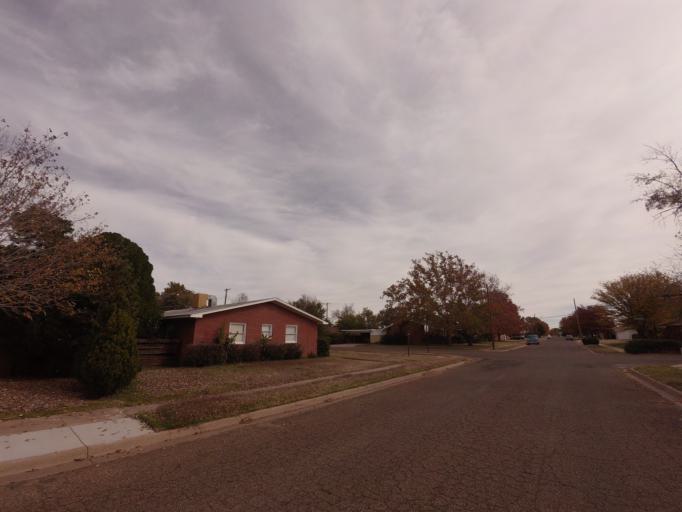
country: US
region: New Mexico
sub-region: Curry County
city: Clovis
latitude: 34.4230
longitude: -103.2099
